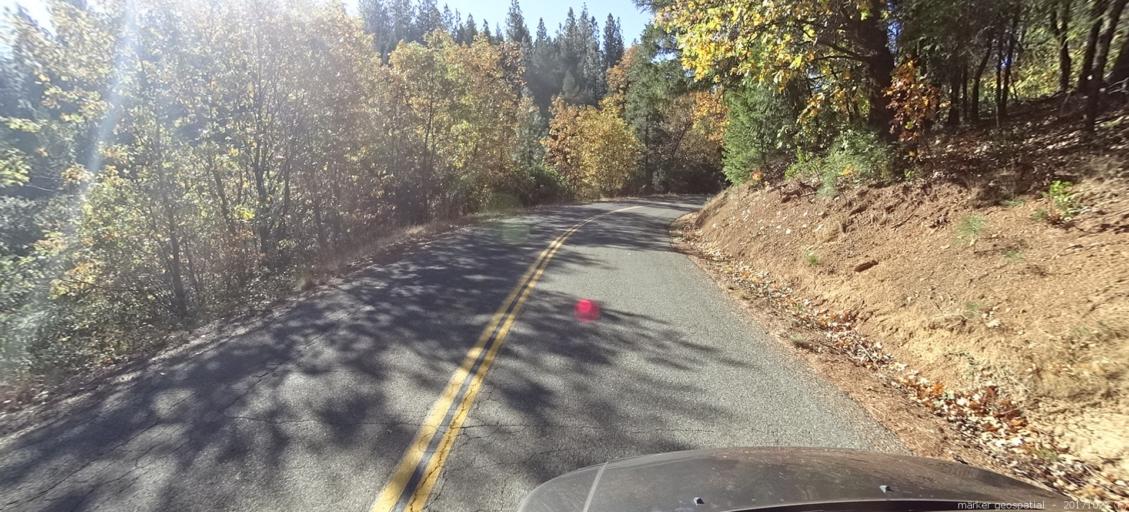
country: US
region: California
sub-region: Shasta County
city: Burney
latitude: 40.8220
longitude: -121.9590
